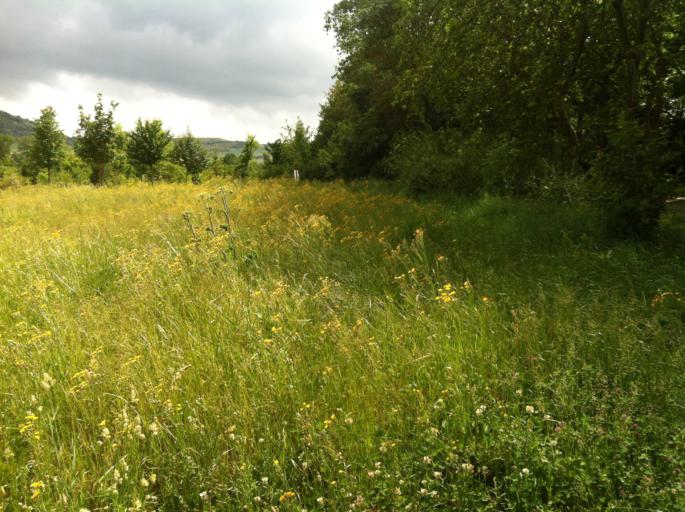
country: ES
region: Basque Country
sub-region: Provincia de Alava
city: Gasteiz / Vitoria
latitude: 42.8308
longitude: -2.6662
